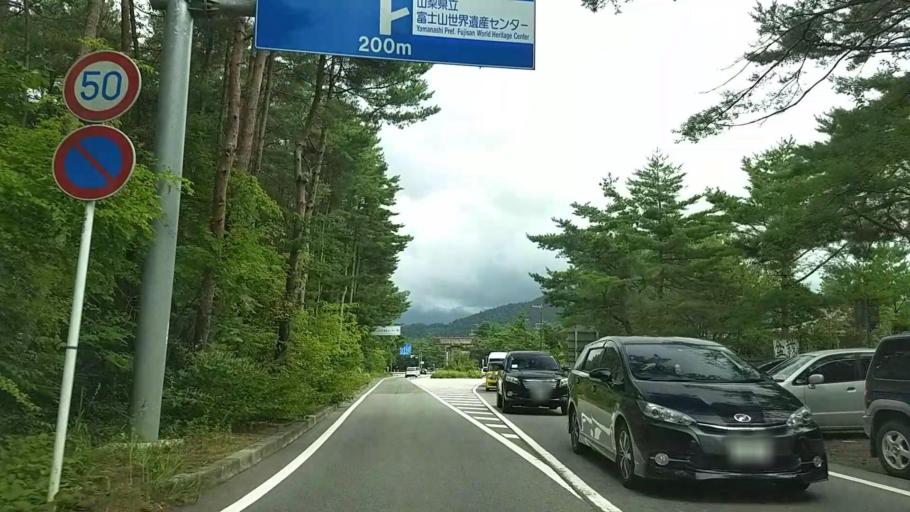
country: JP
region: Yamanashi
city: Fujikawaguchiko
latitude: 35.4846
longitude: 138.7698
